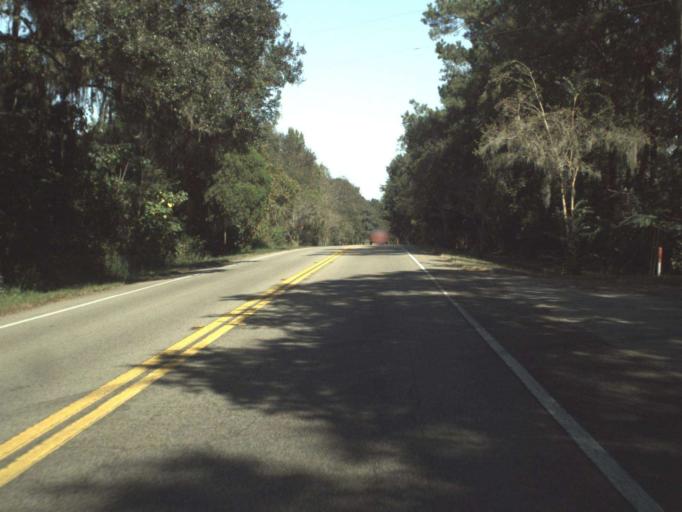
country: US
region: Florida
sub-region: Leon County
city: Tallahassee
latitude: 30.5001
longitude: -84.1003
